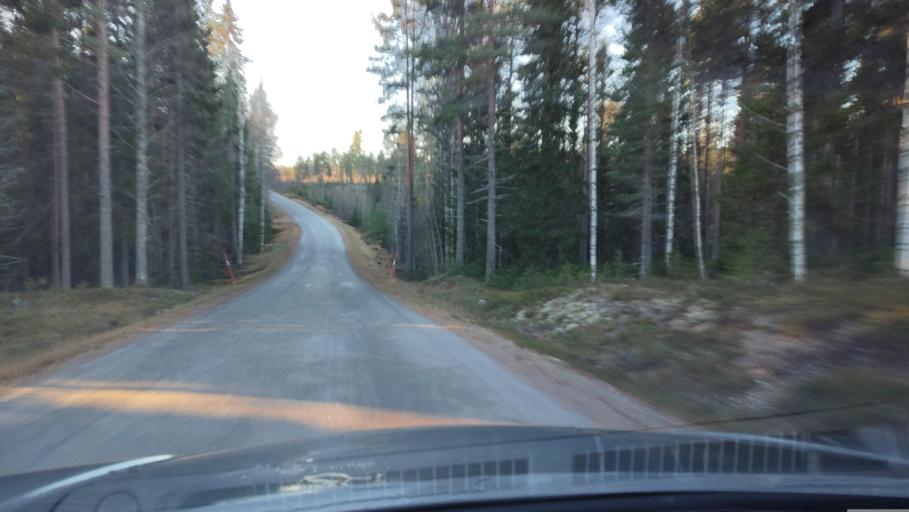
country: SE
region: Vaesterbotten
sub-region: Skelleftea Kommun
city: Viken
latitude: 64.7130
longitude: 20.9094
